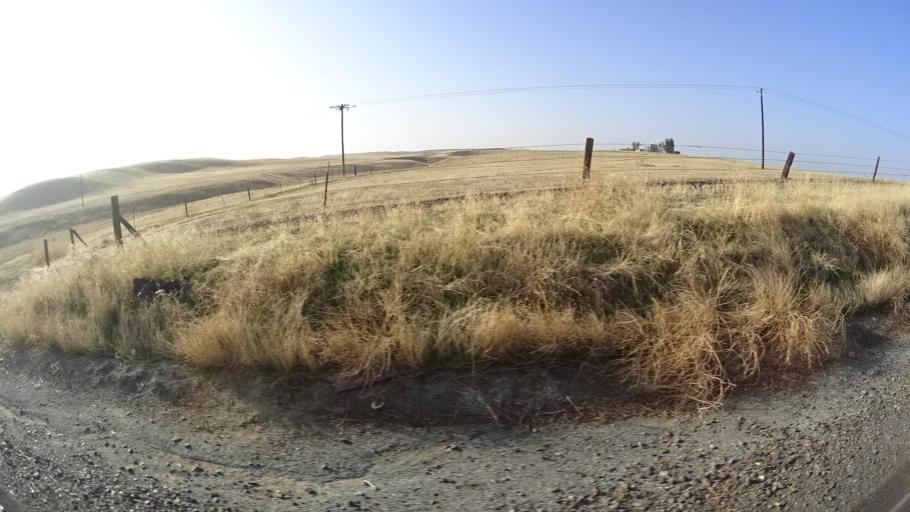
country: US
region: California
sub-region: Tulare County
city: Richgrove
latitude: 35.7607
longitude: -119.0305
